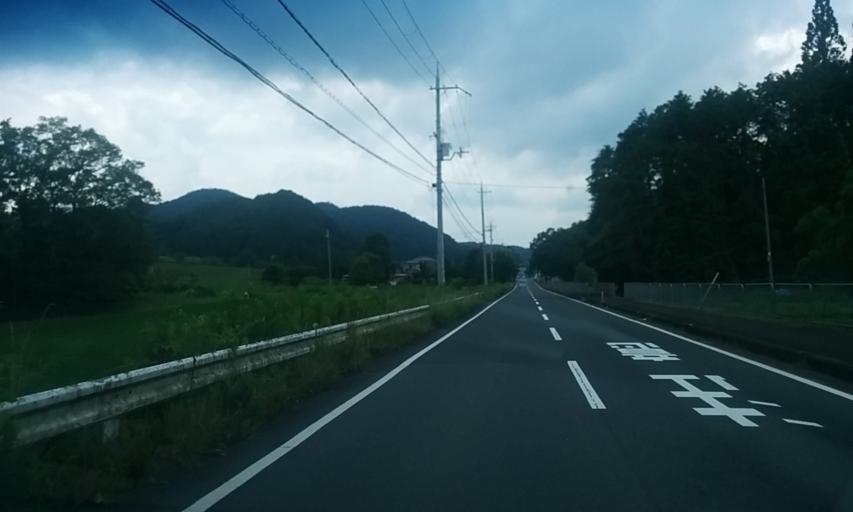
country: JP
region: Kyoto
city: Ayabe
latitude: 35.1576
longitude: 135.4196
